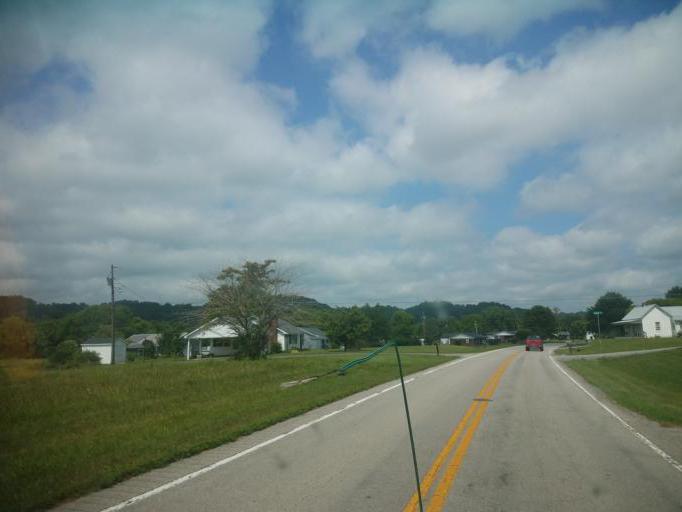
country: US
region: Kentucky
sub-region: Cumberland County
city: Burkesville
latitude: 36.8224
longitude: -85.4790
